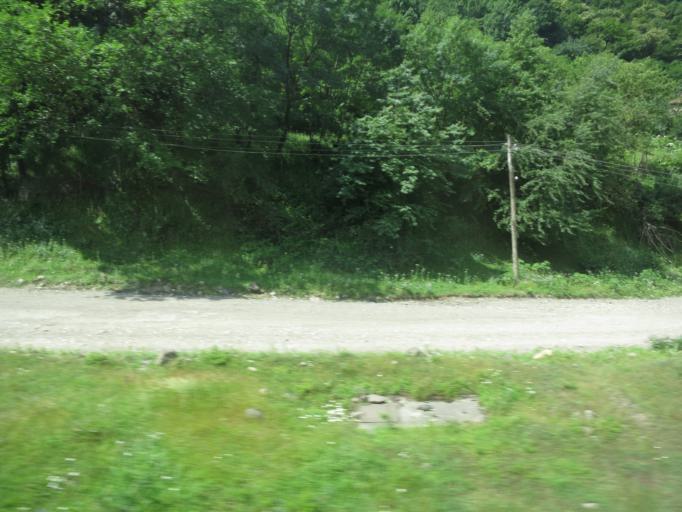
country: GE
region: Imereti
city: Kharagauli
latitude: 42.0044
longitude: 43.2219
